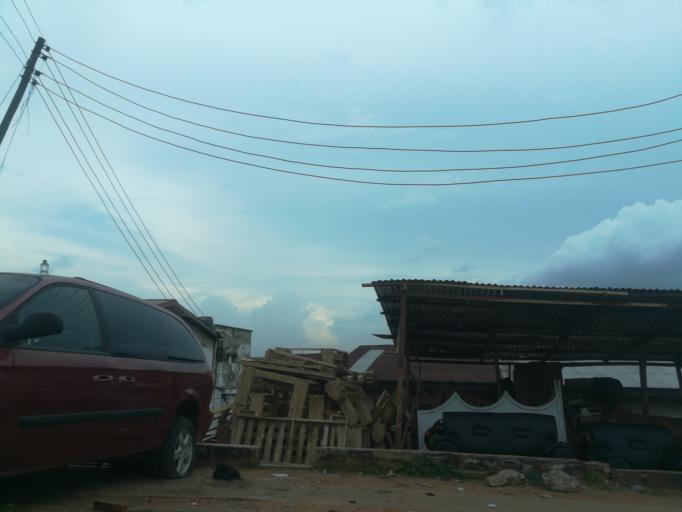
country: NG
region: Oyo
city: Ibadan
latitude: 7.4277
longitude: 3.8912
